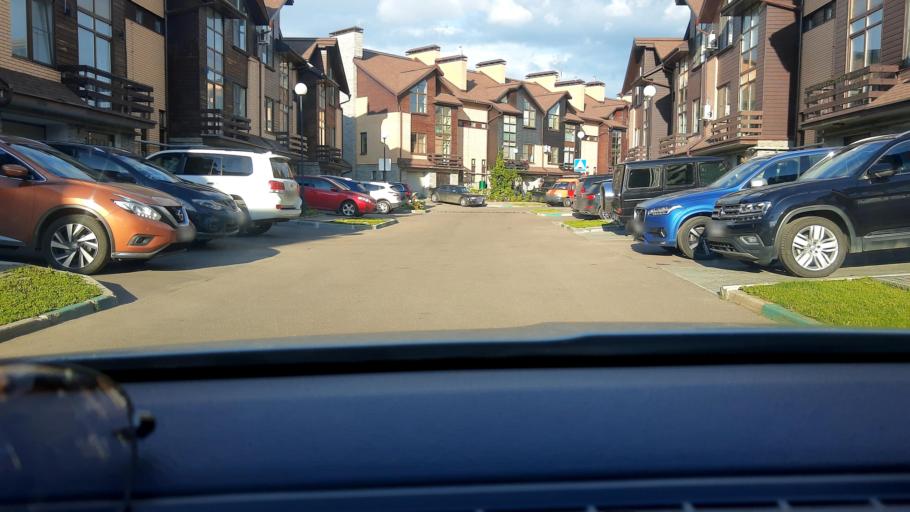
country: RU
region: Moskovskaya
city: Kommunarka
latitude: 55.5276
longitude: 37.4558
